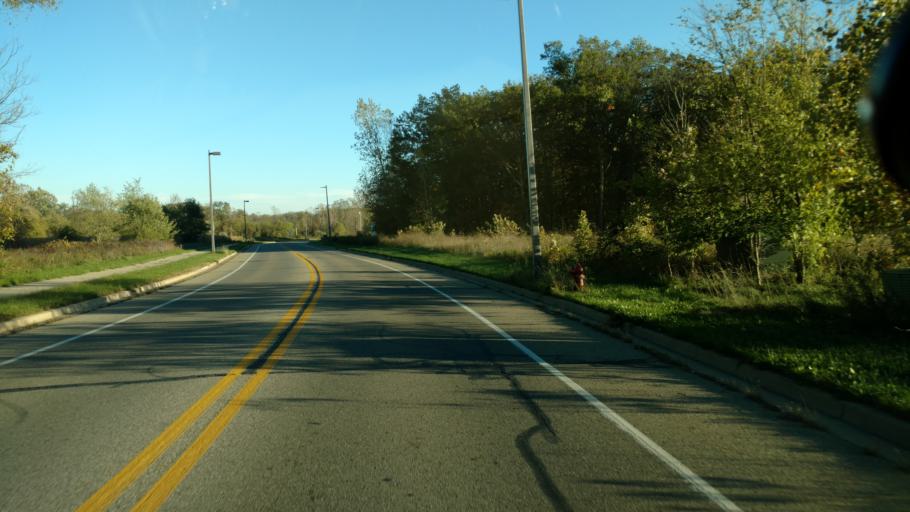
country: US
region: Michigan
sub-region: Ingham County
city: East Lansing
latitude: 42.7776
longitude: -84.5068
